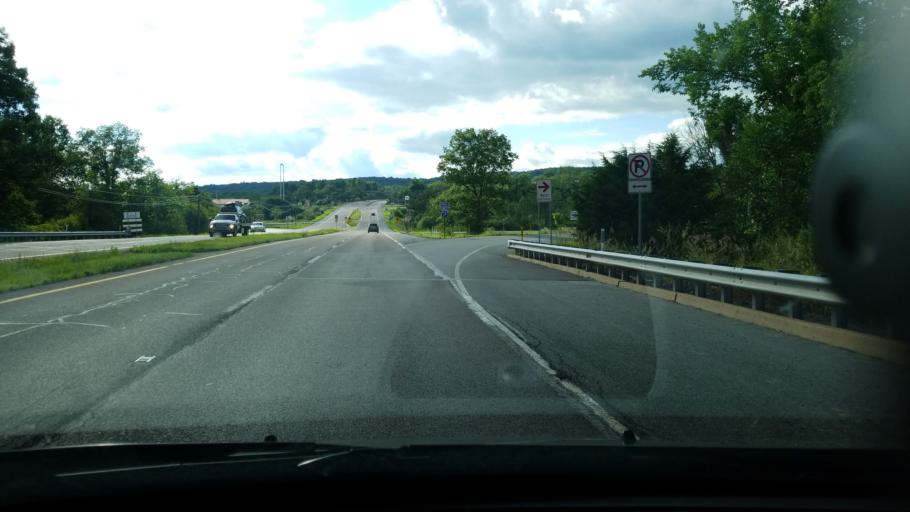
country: US
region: Pennsylvania
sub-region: Northumberland County
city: Riverside
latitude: 40.9963
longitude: -76.6448
